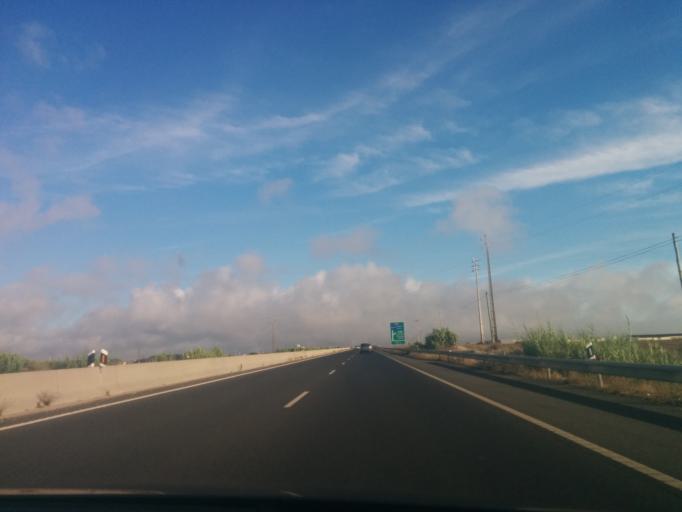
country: PT
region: Leiria
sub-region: Peniche
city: Atouguia da Baleia
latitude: 39.3372
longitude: -9.3369
